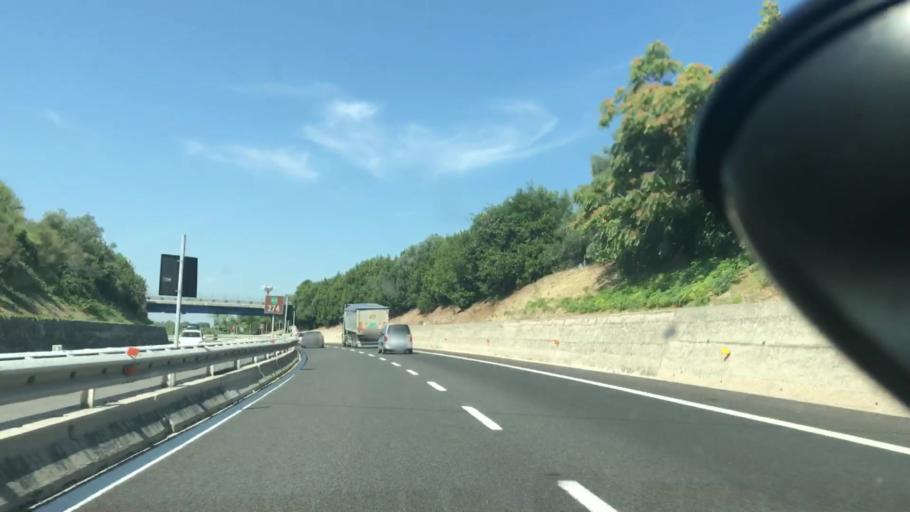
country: IT
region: Abruzzo
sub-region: Provincia di Chieti
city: Casalbordino-Miracoli
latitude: 42.1696
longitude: 14.6239
